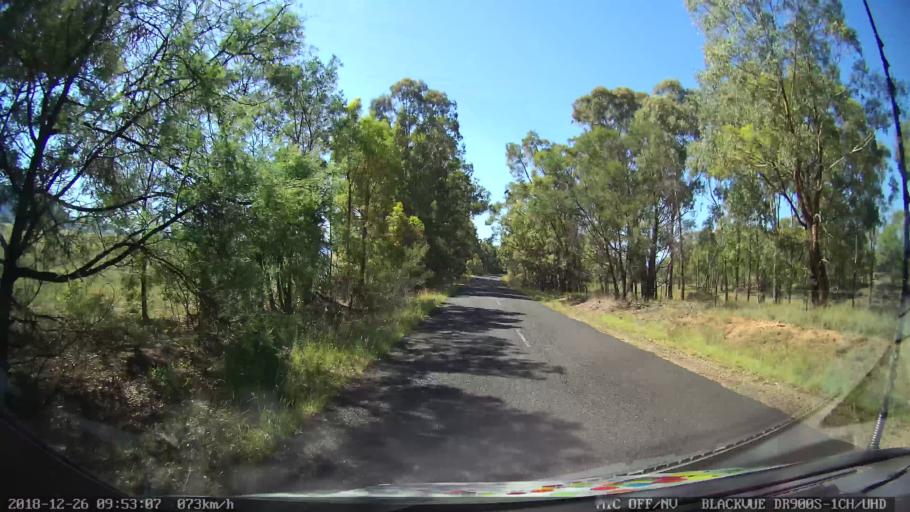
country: AU
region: New South Wales
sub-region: Mid-Western Regional
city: Kandos
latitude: -33.0176
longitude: 150.1520
